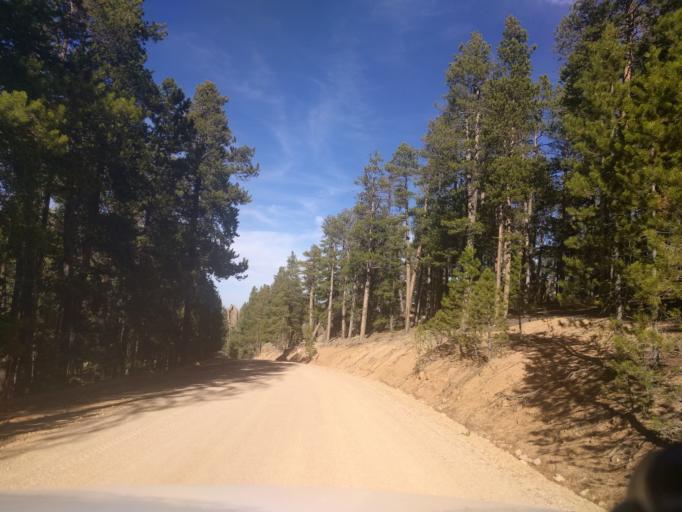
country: US
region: Colorado
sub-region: Douglas County
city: Perry Park
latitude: 39.1980
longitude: -105.0518
